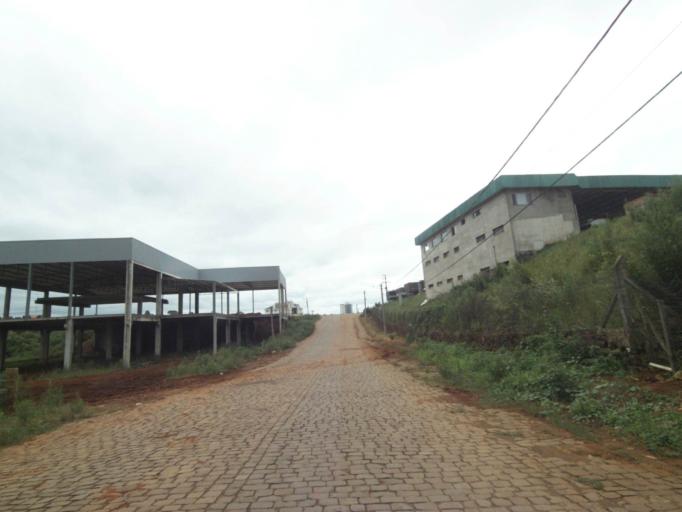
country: BR
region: Rio Grande do Sul
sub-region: Lagoa Vermelha
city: Lagoa Vermelha
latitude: -28.2138
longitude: -51.5088
